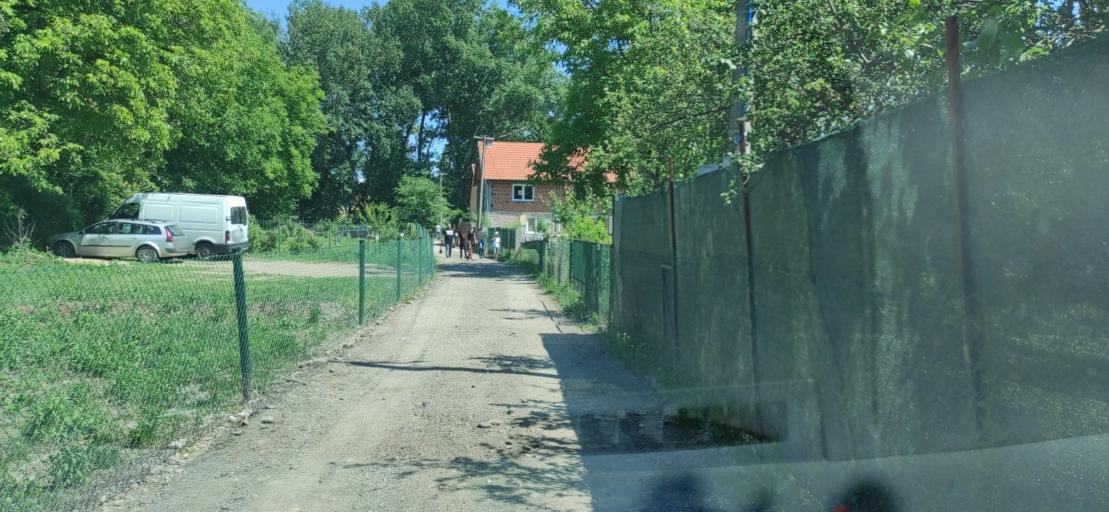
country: RS
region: Central Serbia
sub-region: Nisavski Okrug
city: Nis
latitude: 43.3204
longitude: 21.9553
